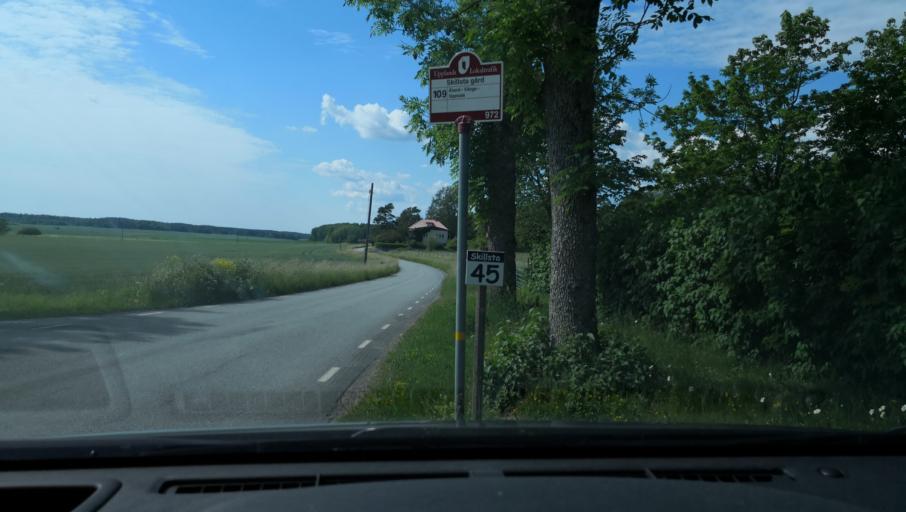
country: SE
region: Uppsala
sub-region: Enkopings Kommun
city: Orsundsbro
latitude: 59.8169
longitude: 17.3353
